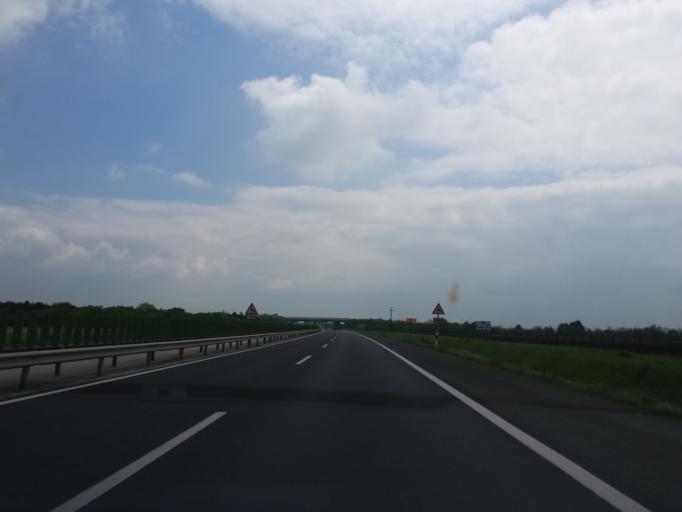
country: AT
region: Burgenland
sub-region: Politischer Bezirk Neusiedl am See
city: Nickelsdorf
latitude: 47.9086
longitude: 17.1379
